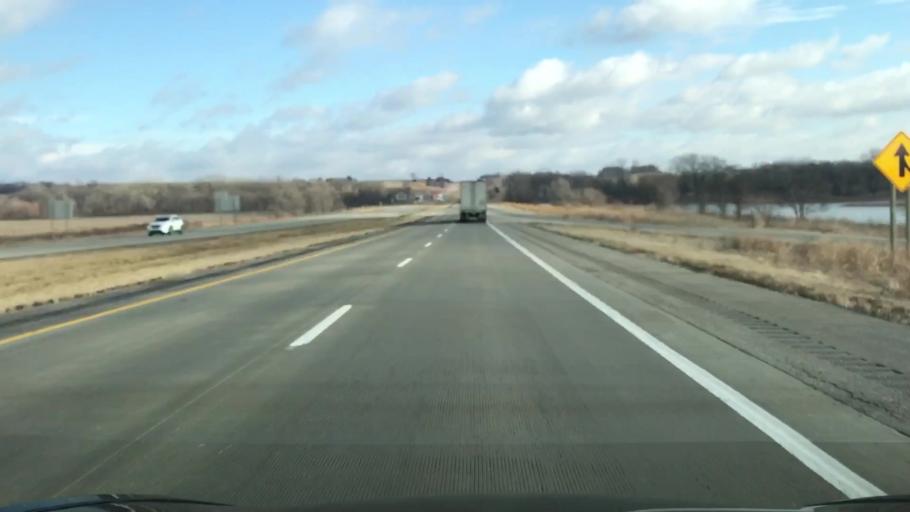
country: US
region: Iowa
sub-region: Cass County
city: Atlantic
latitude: 41.4971
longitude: -94.9411
